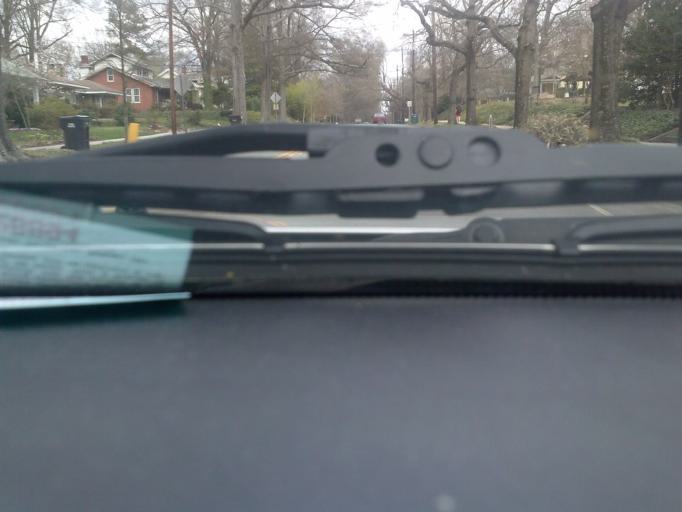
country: US
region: North Carolina
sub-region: Durham County
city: Durham
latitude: 36.0174
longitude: -78.9272
